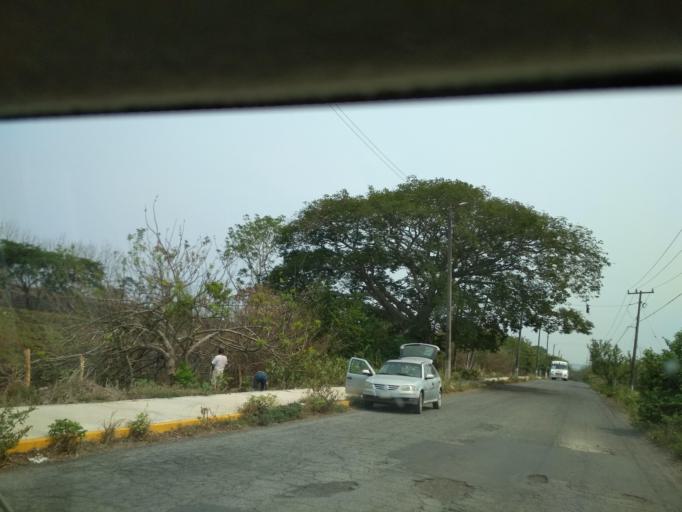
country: MX
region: Veracruz
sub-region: Veracruz
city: Delfino Victoria (Santa Fe)
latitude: 19.1990
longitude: -96.2755
